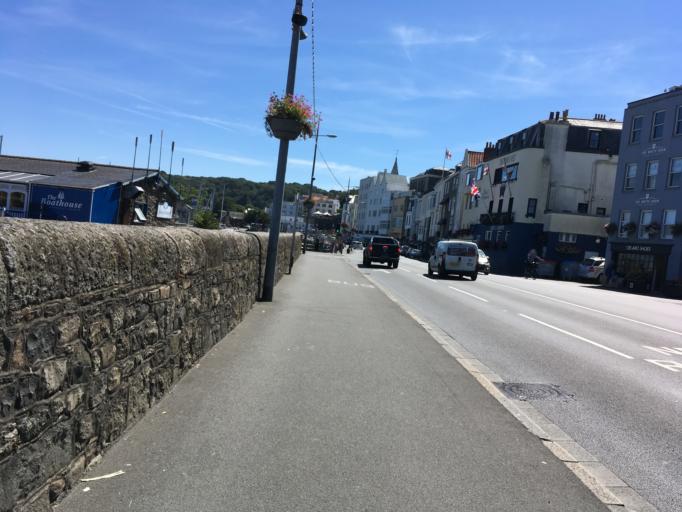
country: GG
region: St Peter Port
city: Saint Peter Port
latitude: 49.4568
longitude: -2.5352
